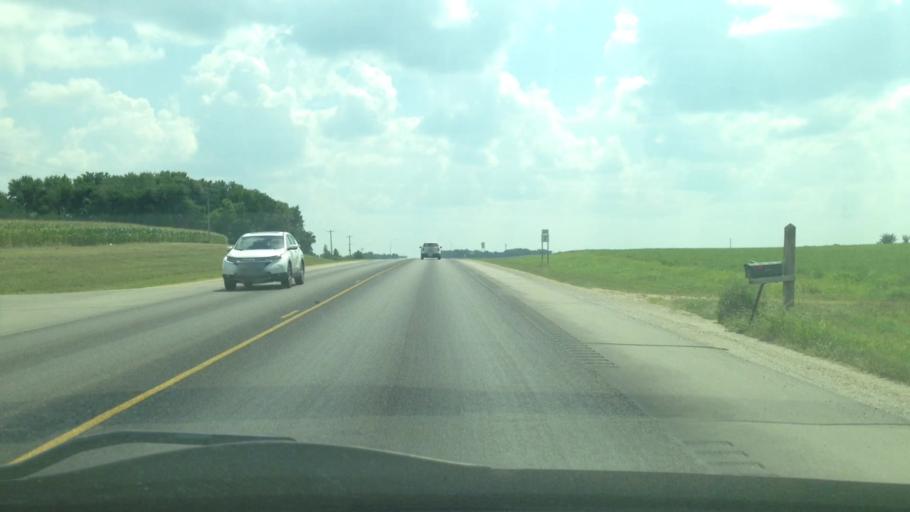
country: US
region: Minnesota
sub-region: Mower County
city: Grand Meadow
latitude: 43.7435
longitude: -92.4794
